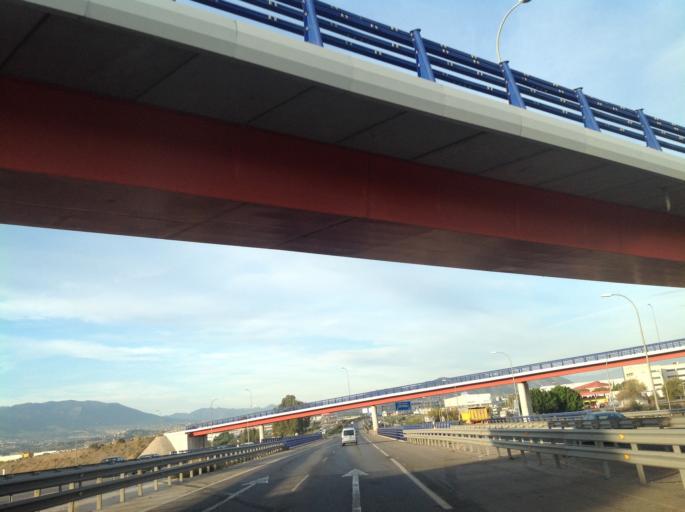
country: ES
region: Andalusia
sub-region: Provincia de Malaga
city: Alhaurin de la Torre
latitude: 36.7127
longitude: -4.5082
